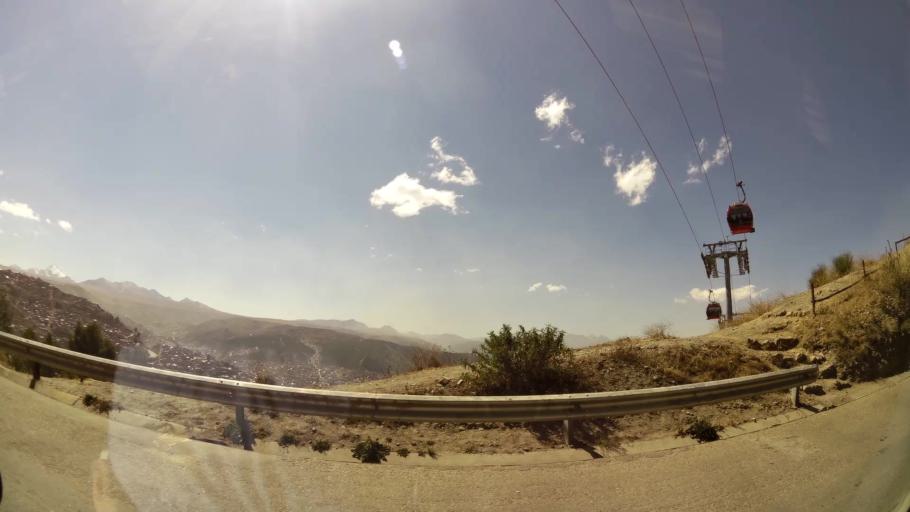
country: BO
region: La Paz
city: La Paz
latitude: -16.4974
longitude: -68.1635
